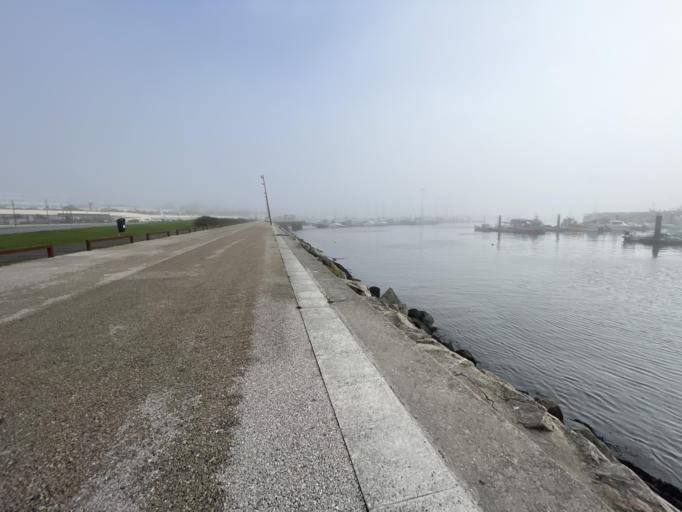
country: PT
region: Porto
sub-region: Povoa de Varzim
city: Povoa de Varzim
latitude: 41.3773
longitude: -8.7664
